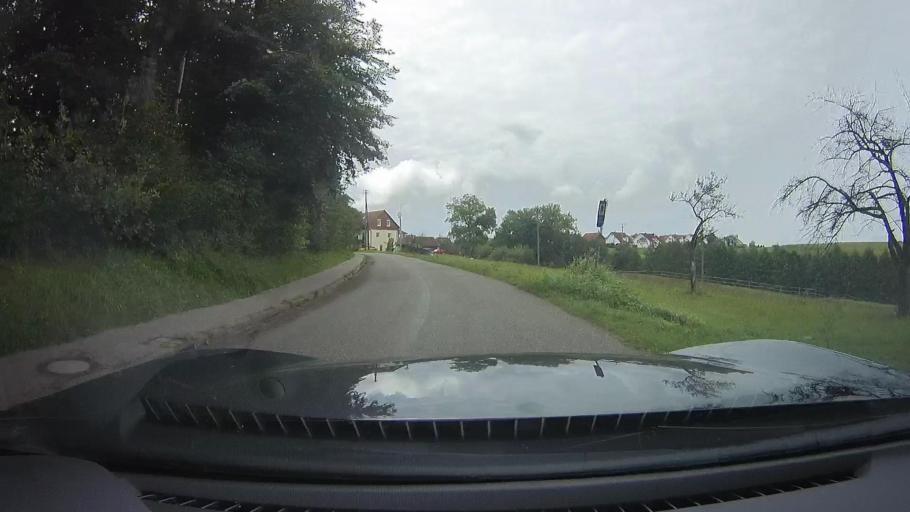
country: DE
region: Baden-Wuerttemberg
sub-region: Regierungsbezirk Stuttgart
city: Althutte
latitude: 48.9468
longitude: 9.5521
